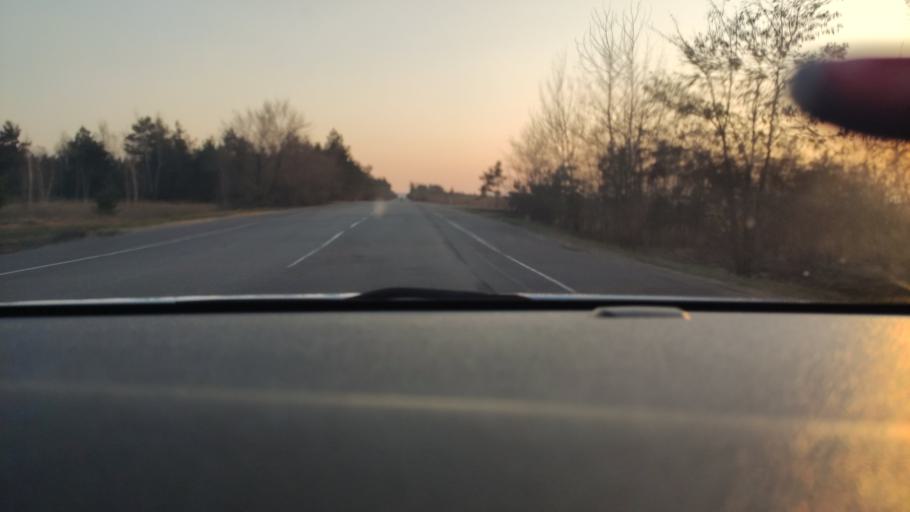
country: RU
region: Voronezj
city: Kolodeznyy
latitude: 51.3699
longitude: 39.2038
